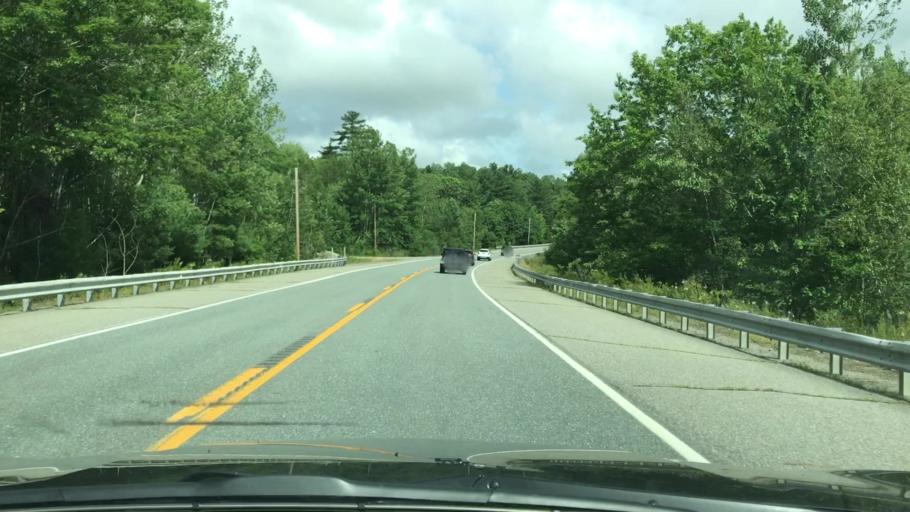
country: US
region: Maine
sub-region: Hancock County
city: Surry
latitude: 44.5636
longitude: -68.5919
